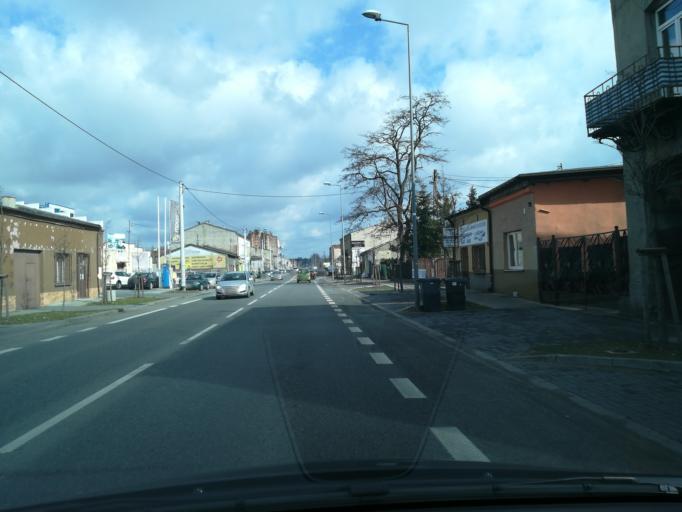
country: PL
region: Silesian Voivodeship
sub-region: Czestochowa
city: Czestochowa
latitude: 50.8195
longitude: 19.1308
